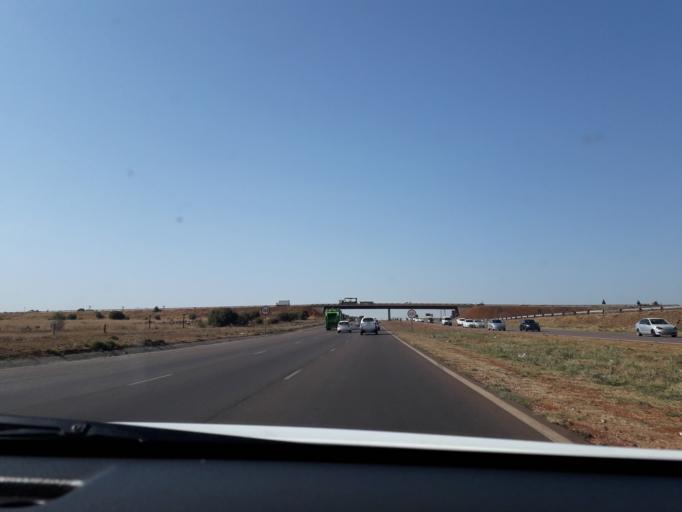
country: ZA
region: Gauteng
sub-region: City of Tshwane Metropolitan Municipality
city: Centurion
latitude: -25.8191
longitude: 28.1824
